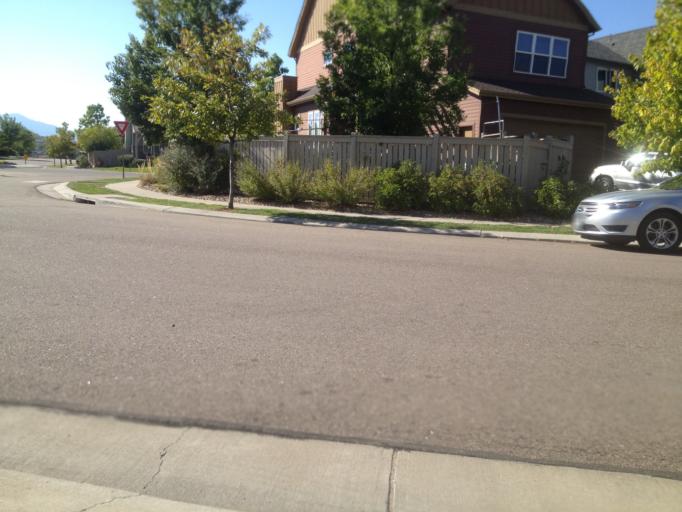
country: US
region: Colorado
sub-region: Boulder County
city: Louisville
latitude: 39.9934
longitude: -105.1230
